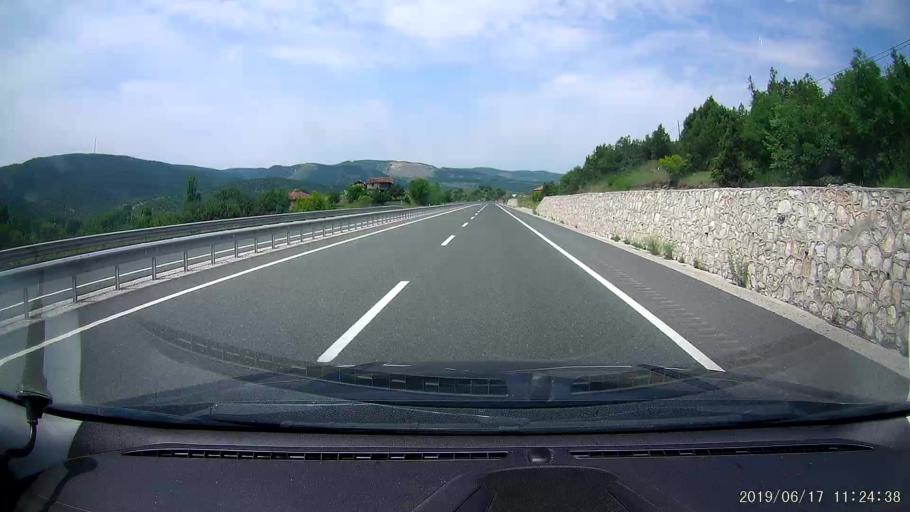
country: TR
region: Cankiri
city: Ilgaz
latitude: 40.8853
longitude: 33.6989
